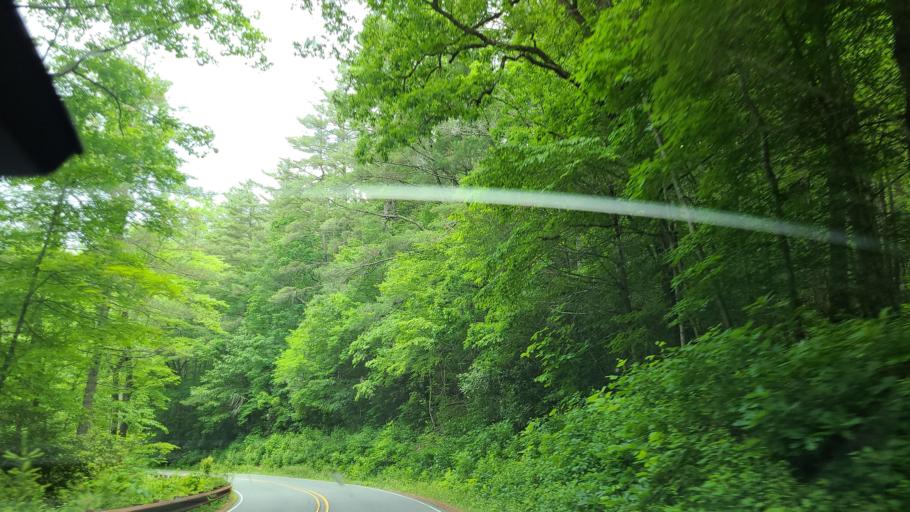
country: US
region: North Carolina
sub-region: Macon County
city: Franklin
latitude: 35.1022
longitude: -83.2632
